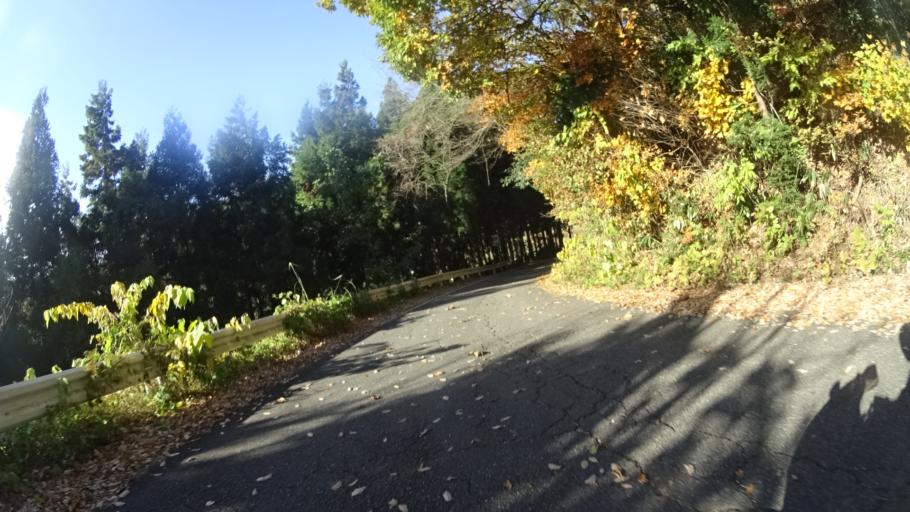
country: JP
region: Niigata
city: Yoshida-kasugacho
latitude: 37.6560
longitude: 138.8128
